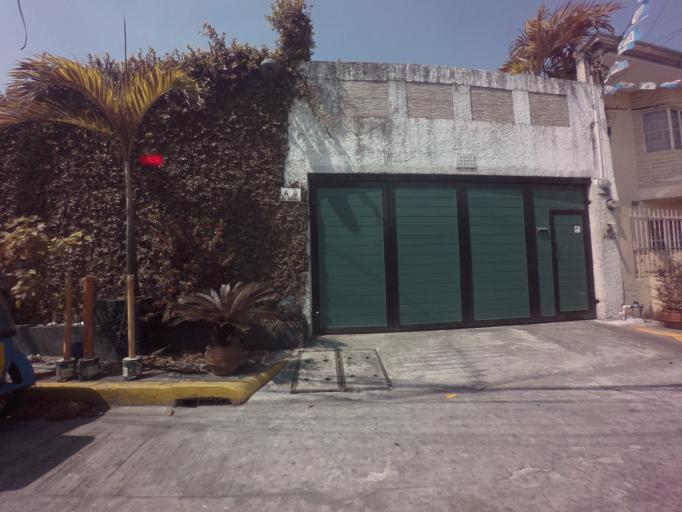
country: PH
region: Metro Manila
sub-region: Makati City
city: Makati City
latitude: 14.5724
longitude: 121.0114
